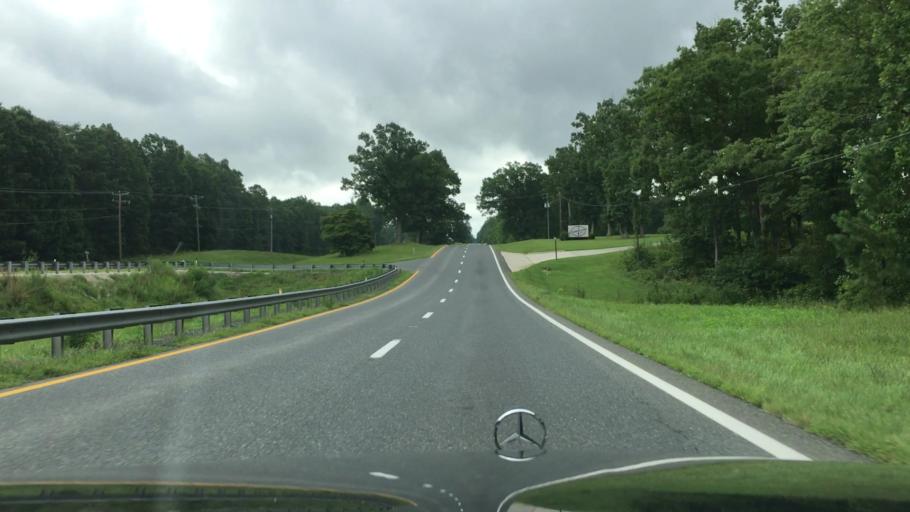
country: US
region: Virginia
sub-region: Appomattox County
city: Appomattox
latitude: 37.3011
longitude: -78.7449
